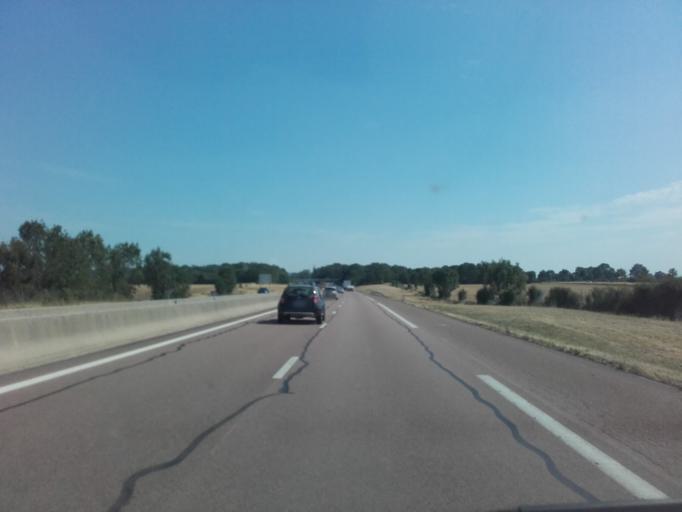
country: FR
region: Bourgogne
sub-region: Departement de la Cote-d'Or
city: Pouilly-en-Auxois
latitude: 47.2299
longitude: 4.5858
